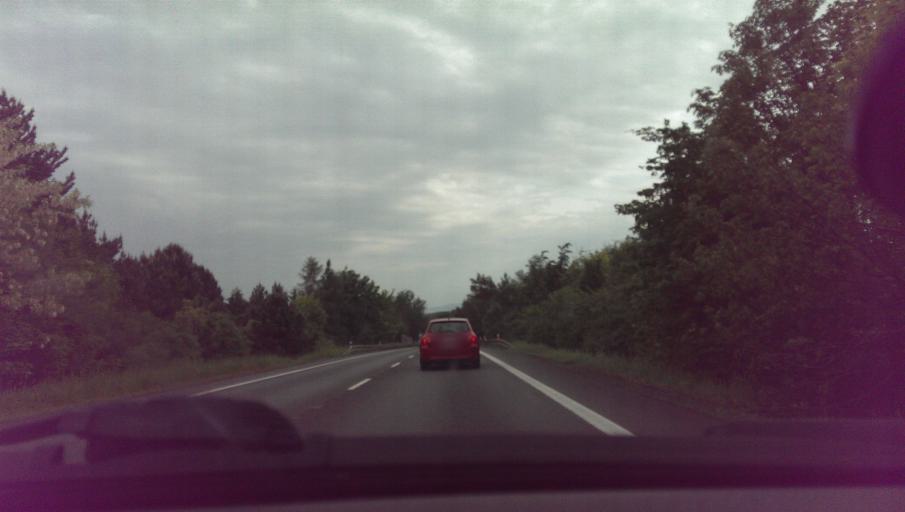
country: CZ
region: Zlin
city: Buchlovice
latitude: 49.0868
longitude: 17.3296
